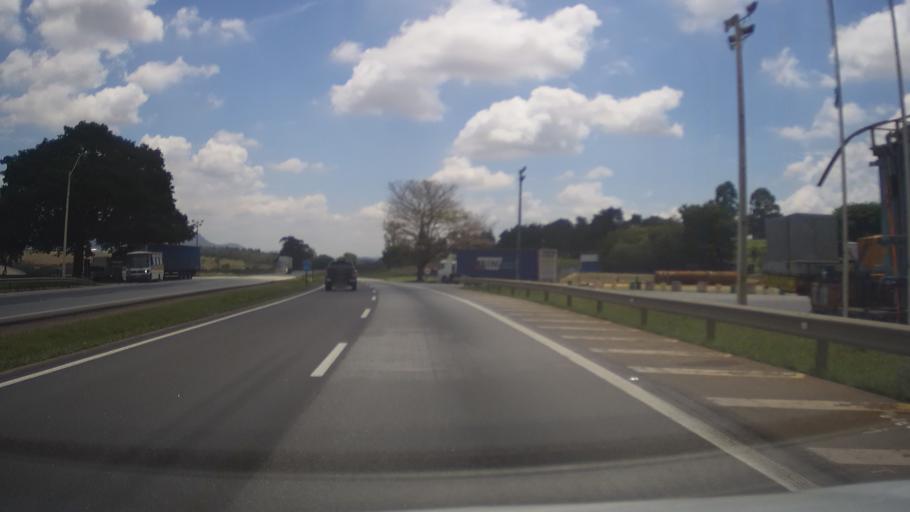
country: BR
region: Minas Gerais
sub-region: Sao Goncalo Do Sapucai
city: Sao Goncalo do Sapucai
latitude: -21.9455
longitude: -45.6201
